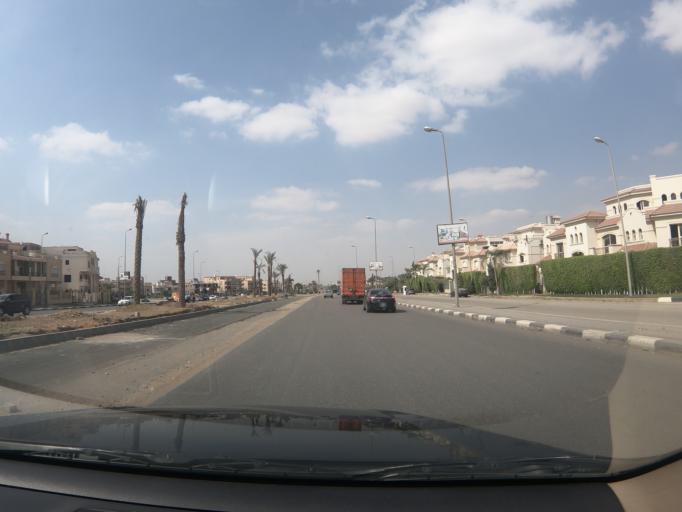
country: EG
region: Muhafazat al Qalyubiyah
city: Al Khankah
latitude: 30.0528
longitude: 31.4751
